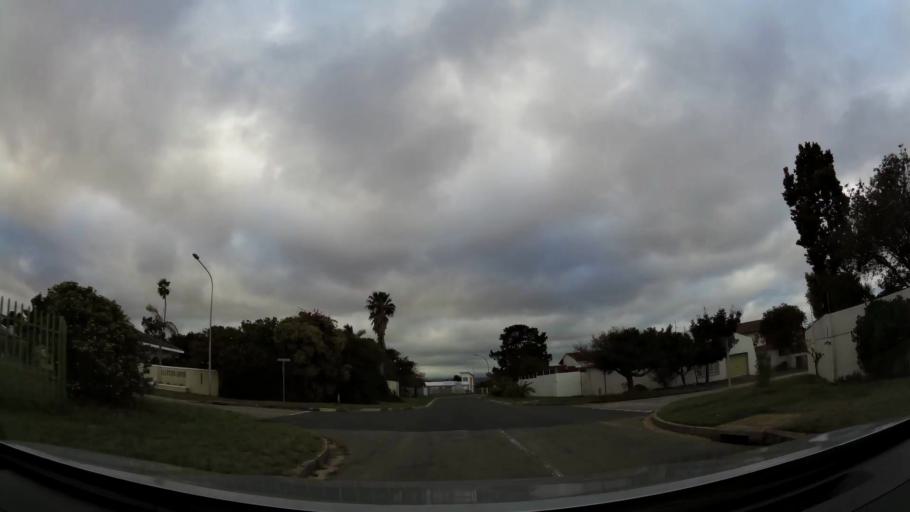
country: ZA
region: Western Cape
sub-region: Eden District Municipality
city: Plettenberg Bay
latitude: -34.0498
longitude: 23.3637
